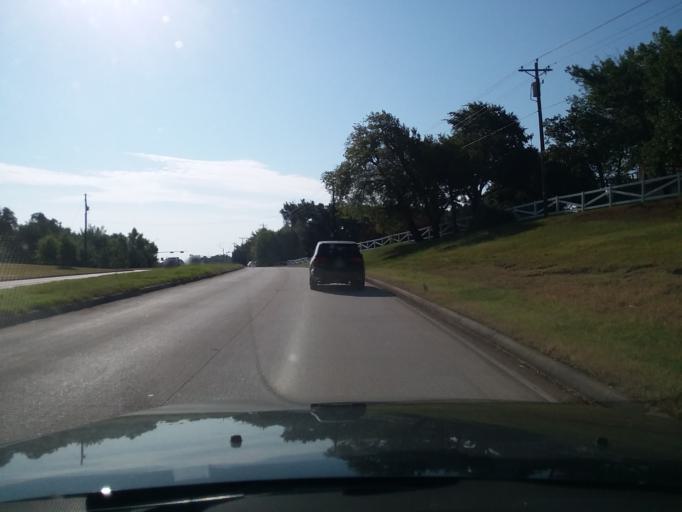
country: US
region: Texas
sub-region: Denton County
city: Bartonville
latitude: 33.0740
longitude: -97.1257
